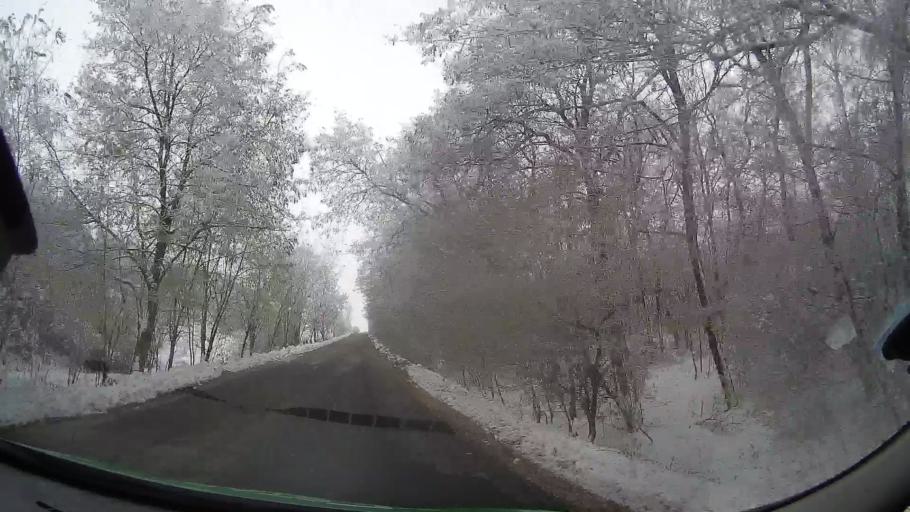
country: RO
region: Bacau
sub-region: Comuna Glavanesti
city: Frumuselu
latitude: 46.2640
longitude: 27.3259
